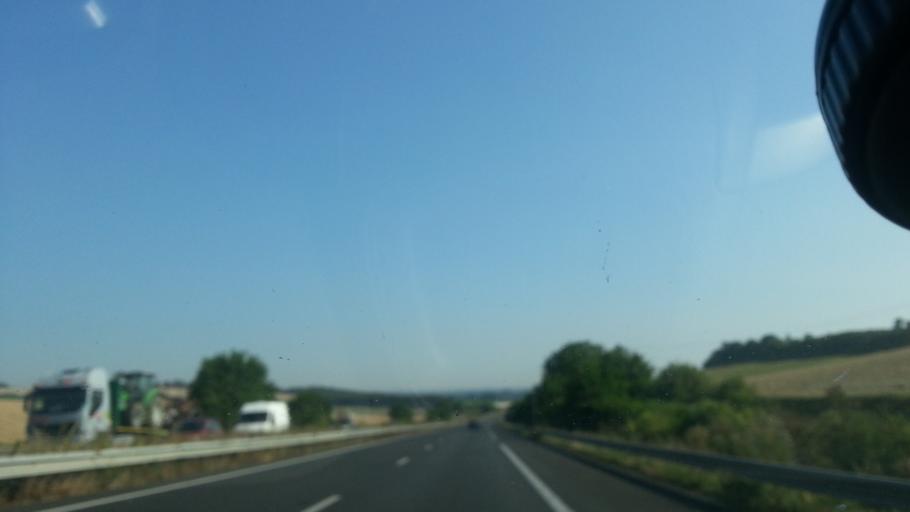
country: FR
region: Poitou-Charentes
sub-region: Departement de la Vienne
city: Les Ormes
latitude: 46.9910
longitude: 0.5493
